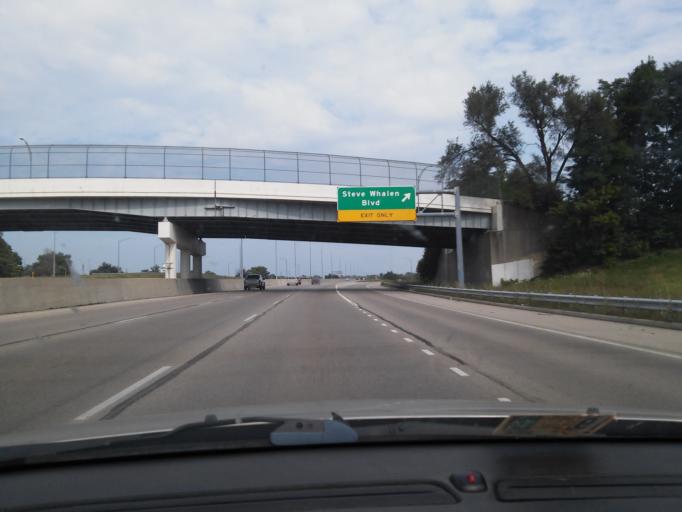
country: US
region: Ohio
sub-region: Montgomery County
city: Dayton
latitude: 39.7551
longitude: -84.1670
